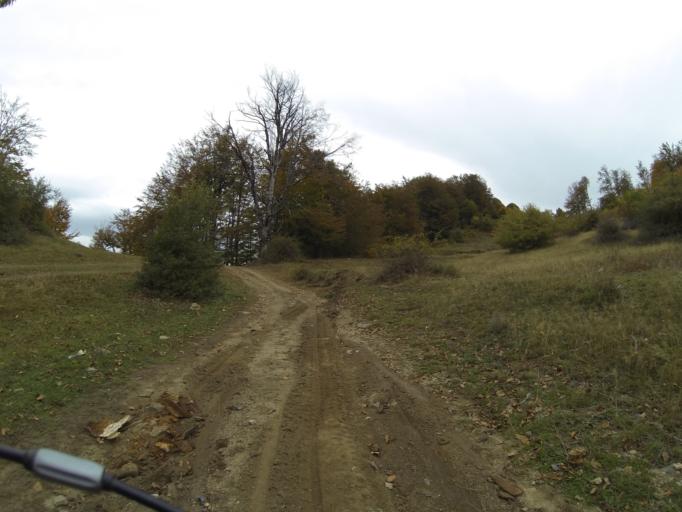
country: RO
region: Gorj
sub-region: Comuna Pades
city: Closani
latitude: 45.0864
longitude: 22.8399
